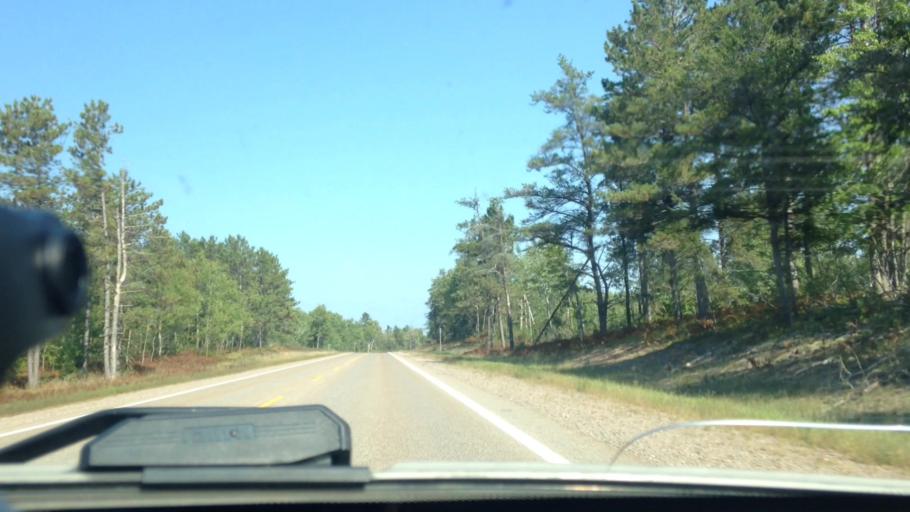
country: US
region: Michigan
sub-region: Mackinac County
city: Saint Ignace
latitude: 46.3552
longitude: -84.8967
